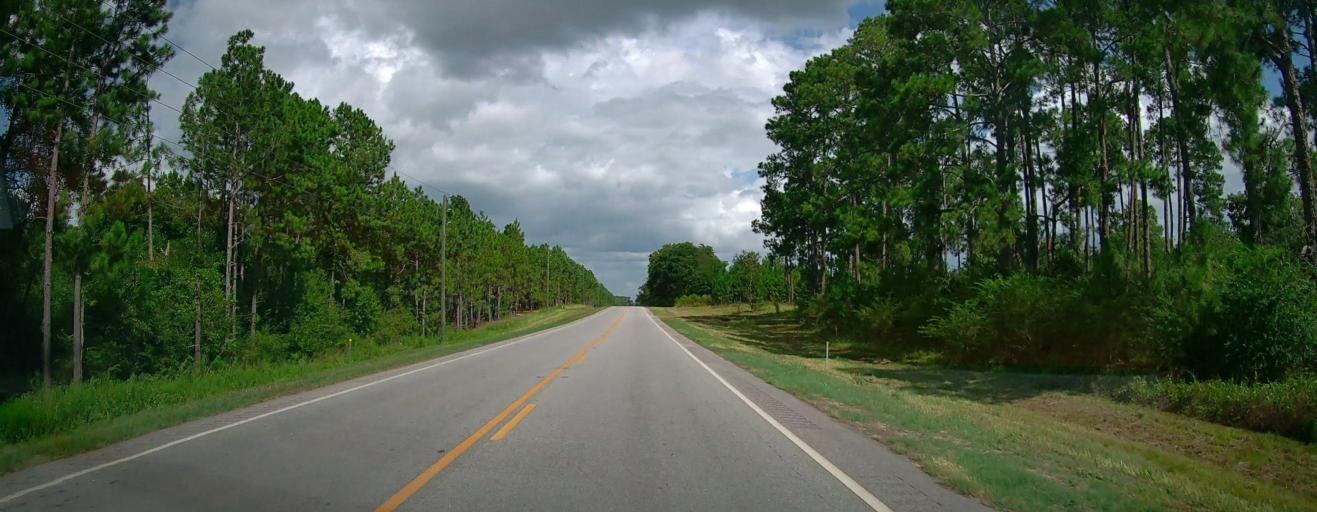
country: US
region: Georgia
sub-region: Coffee County
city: Broxton
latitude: 31.5782
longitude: -83.0534
